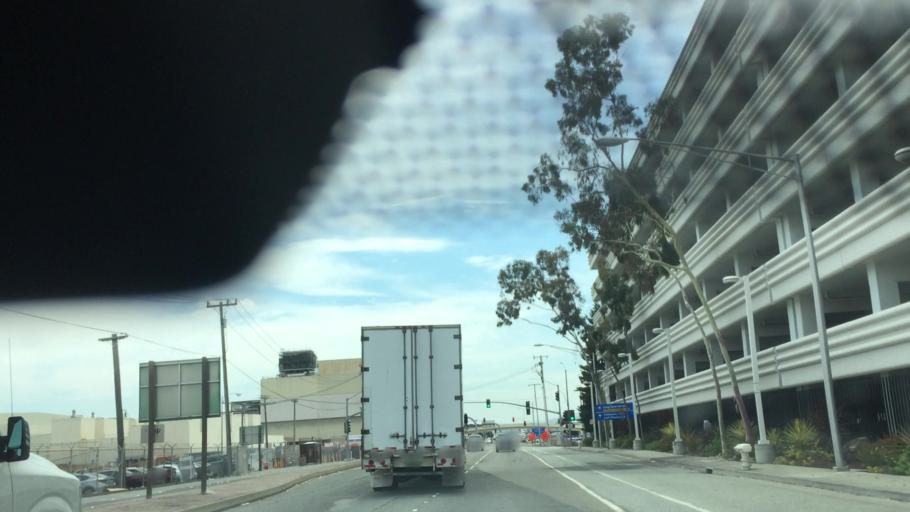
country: US
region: California
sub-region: San Mateo County
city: San Bruno
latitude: 37.6371
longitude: -122.4002
